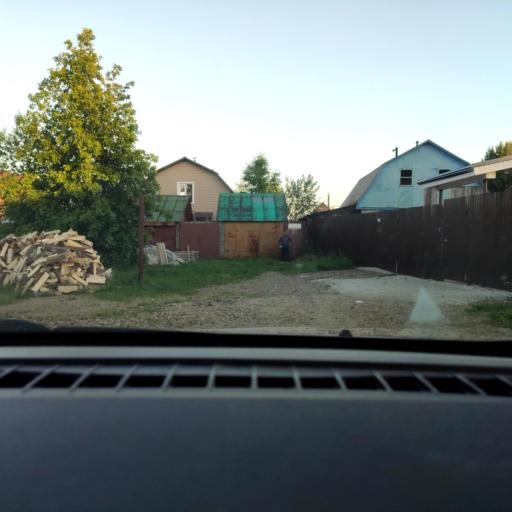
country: RU
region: Perm
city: Polazna
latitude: 58.1743
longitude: 56.4014
